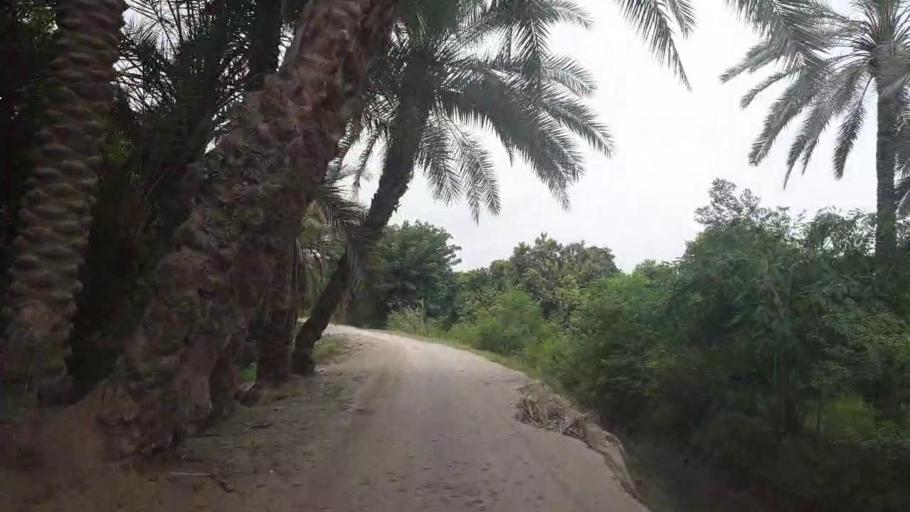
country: PK
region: Sindh
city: Khairpur
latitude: 27.5865
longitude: 68.7141
